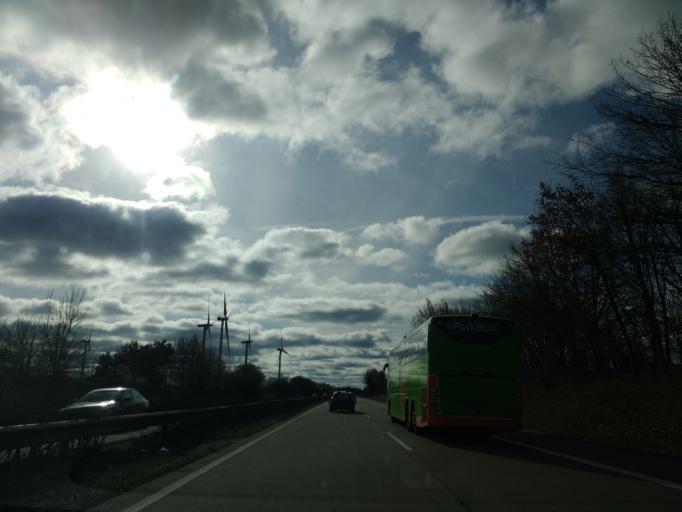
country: DE
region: Lower Saxony
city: Langen
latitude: 53.6406
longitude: 8.6637
